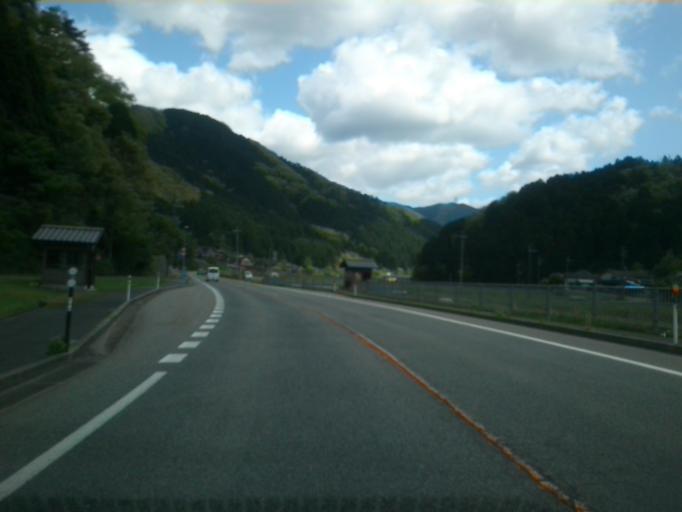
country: JP
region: Kyoto
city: Fukuchiyama
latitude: 35.4303
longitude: 135.0011
